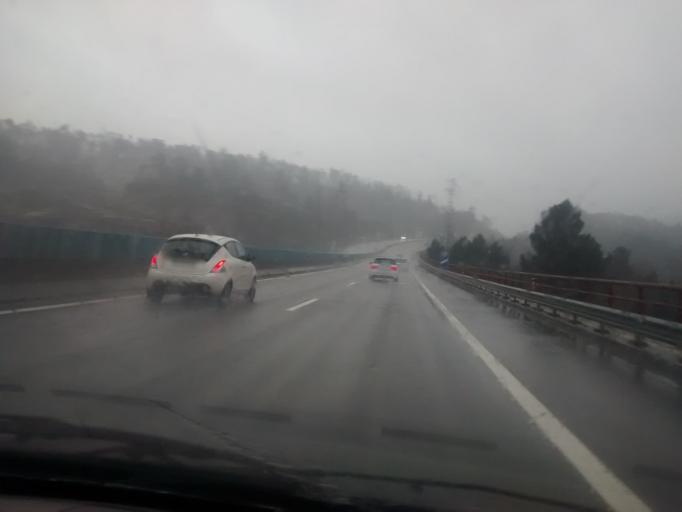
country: PT
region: Braga
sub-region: Braga
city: Braga
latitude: 41.5206
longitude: -8.4458
